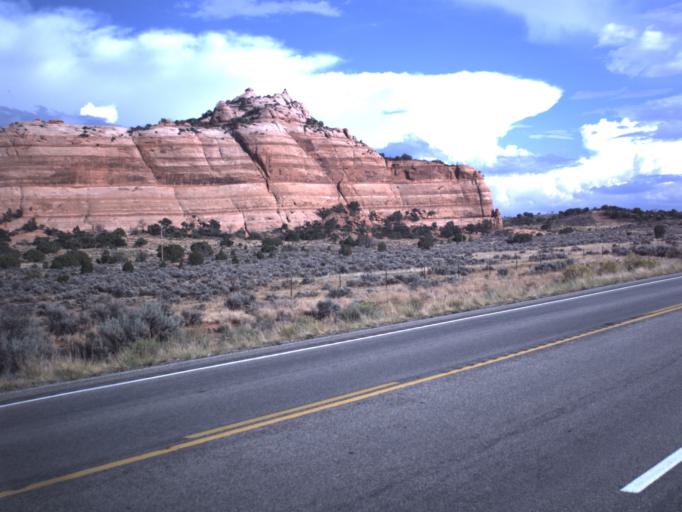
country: US
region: Utah
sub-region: Grand County
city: Moab
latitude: 38.3317
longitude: -109.4306
